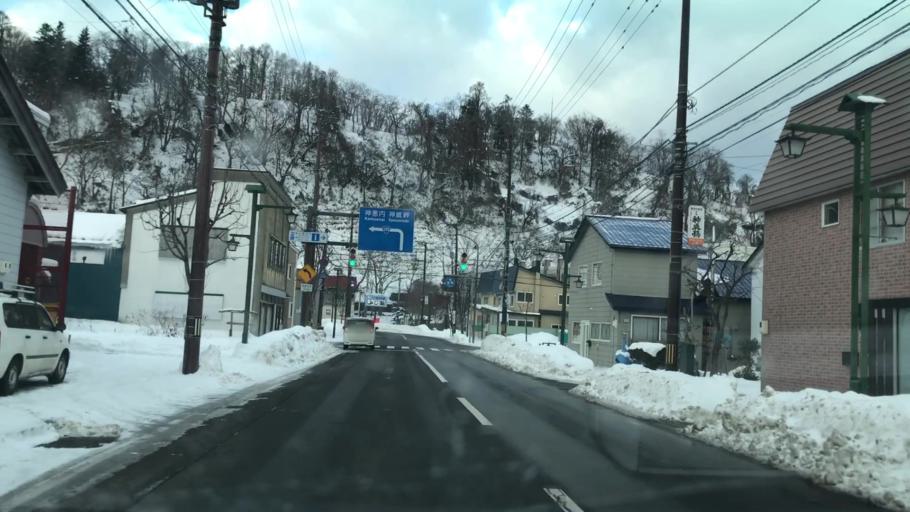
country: JP
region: Hokkaido
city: Yoichi
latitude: 43.2975
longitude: 140.5988
